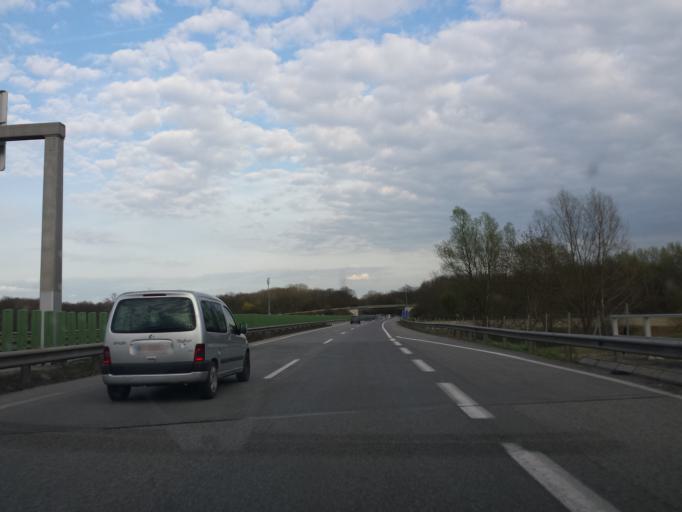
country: AT
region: Lower Austria
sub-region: Politischer Bezirk Tulln
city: Tulln
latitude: 48.3623
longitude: 16.0658
